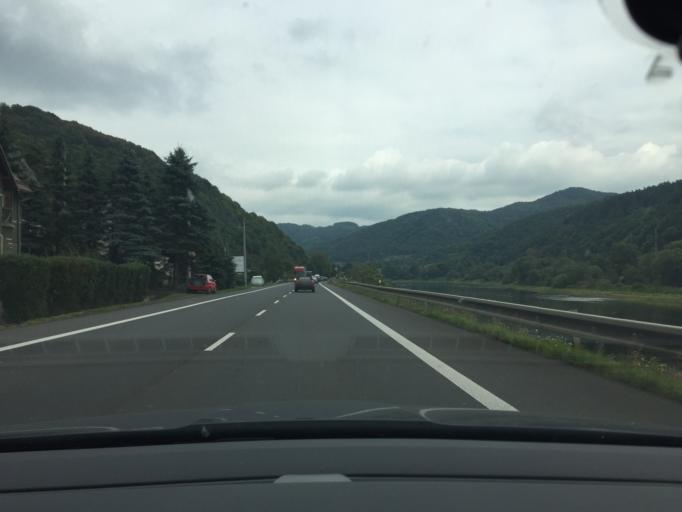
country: CZ
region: Ustecky
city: Povrly
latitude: 50.6845
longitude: 14.1755
